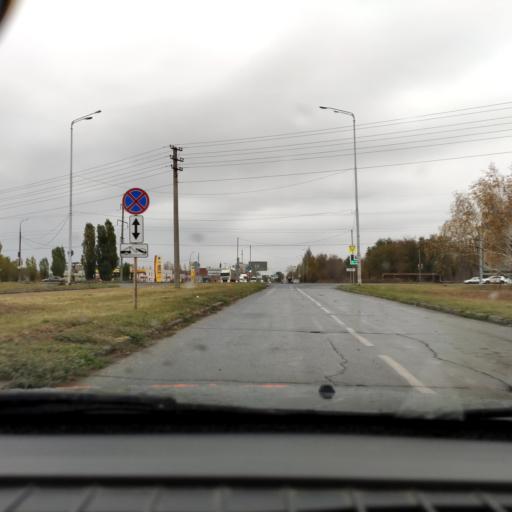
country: RU
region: Samara
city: Tol'yatti
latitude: 53.5612
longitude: 49.2880
